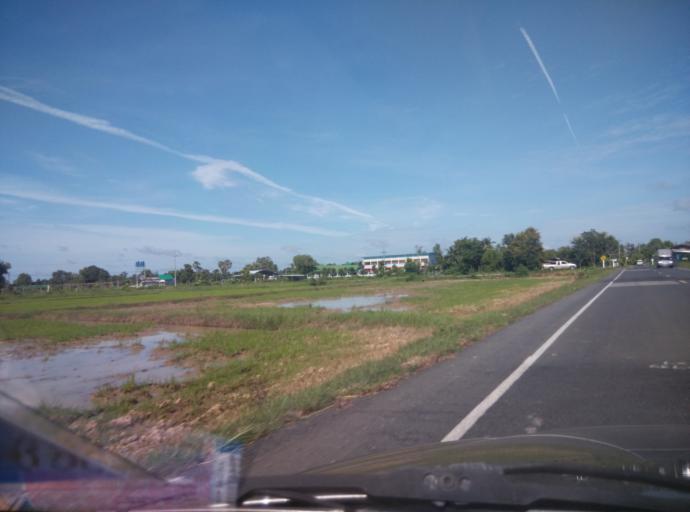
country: TH
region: Sisaket
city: Uthumphon Phisai
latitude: 15.1201
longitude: 104.2275
